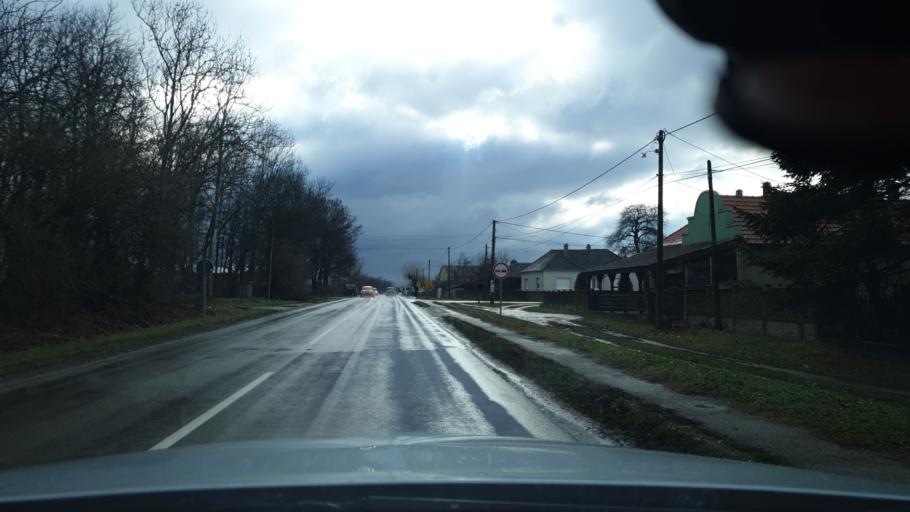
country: RS
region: Central Serbia
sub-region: Branicevski Okrug
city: Malo Crnice
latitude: 44.5323
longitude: 21.3157
